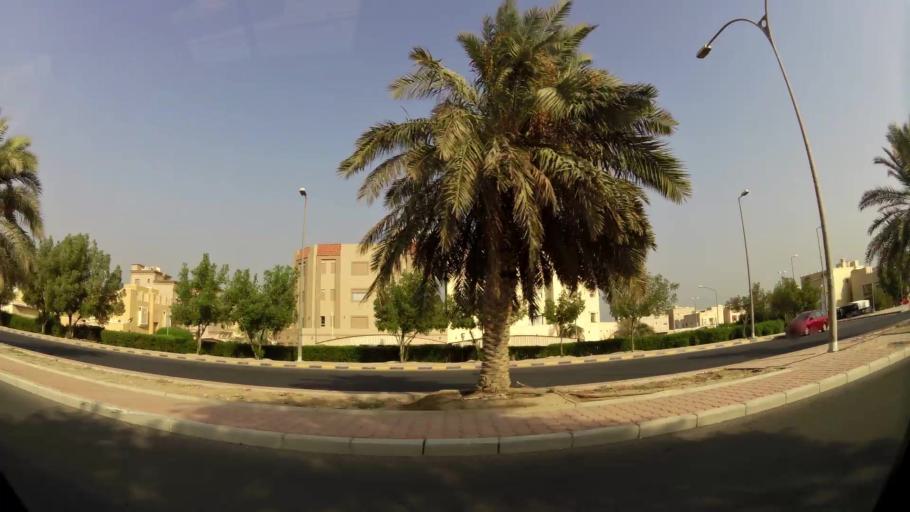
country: KW
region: Al Ahmadi
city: Ar Riqqah
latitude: 29.1293
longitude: 48.1038
